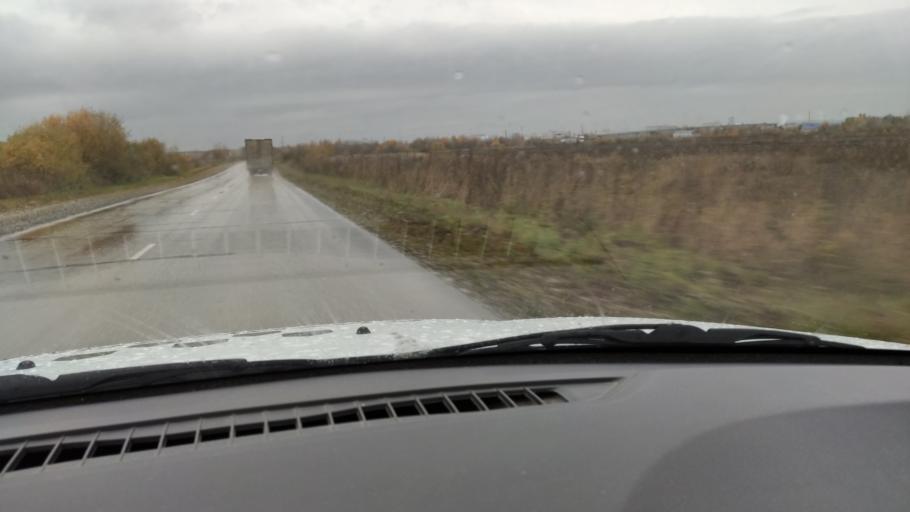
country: RU
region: Perm
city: Kondratovo
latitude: 58.0023
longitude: 56.0655
